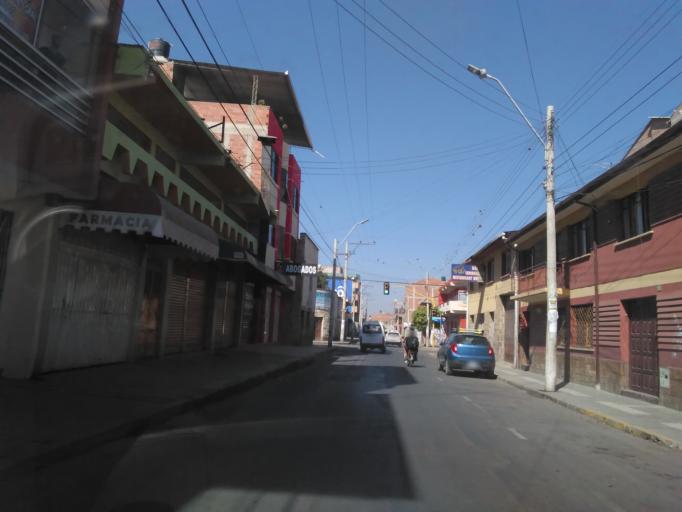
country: BO
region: Cochabamba
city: Sipe Sipe
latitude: -17.3997
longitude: -66.2795
